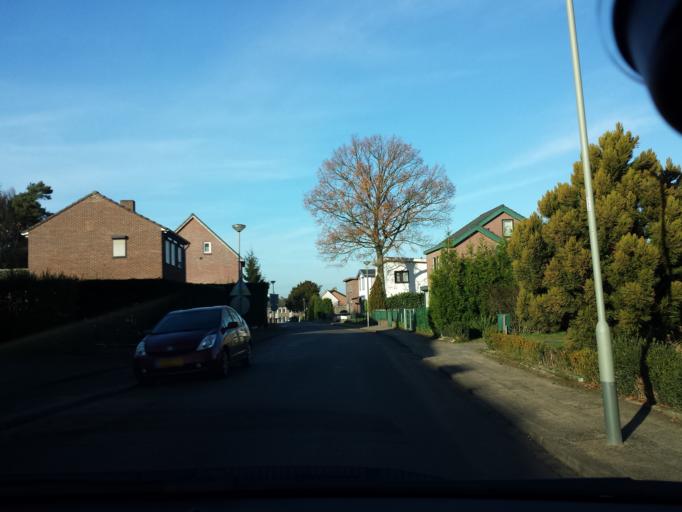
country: NL
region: Limburg
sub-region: Gemeente Onderbanken
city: Schinveld
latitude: 50.9634
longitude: 5.9865
